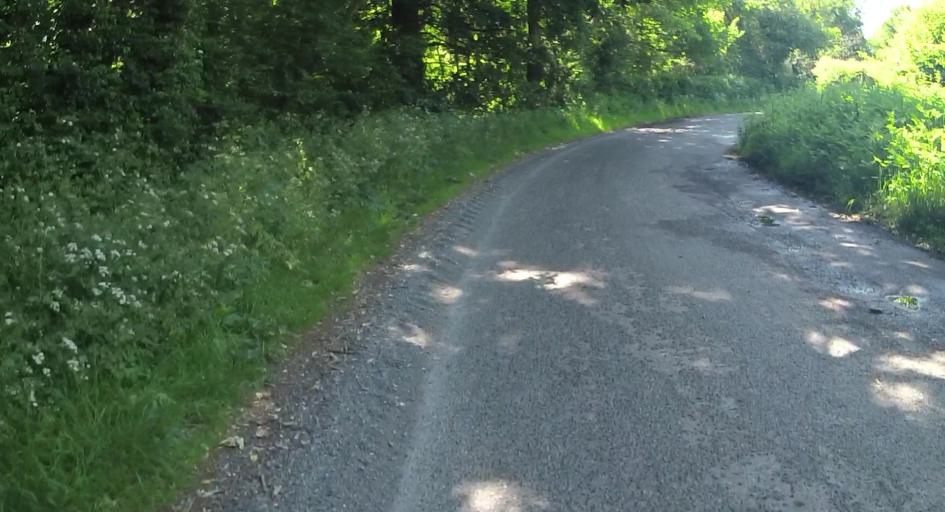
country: GB
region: England
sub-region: West Berkshire
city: Greenham
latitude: 51.3621
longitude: -1.2772
